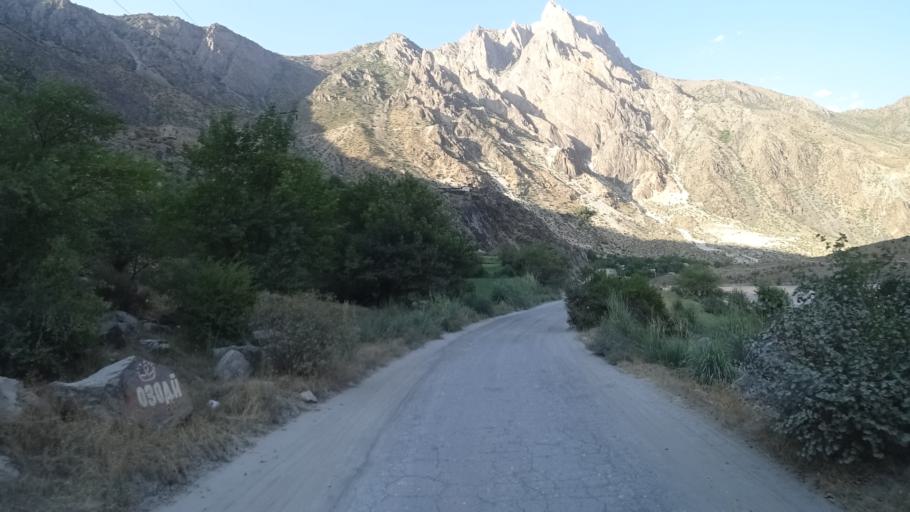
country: AF
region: Badakhshan
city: Maymay
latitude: 38.4893
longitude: 70.9851
